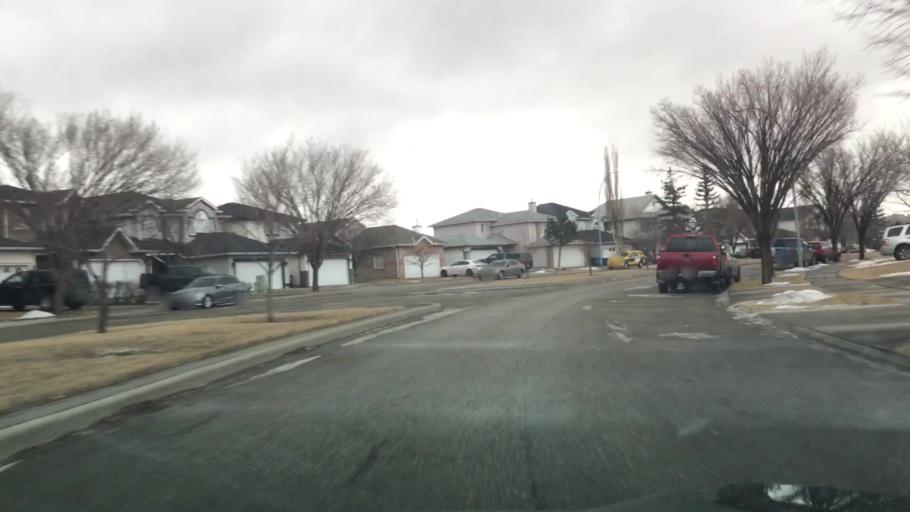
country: CA
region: Alberta
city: Calgary
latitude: 51.1481
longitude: -114.1194
